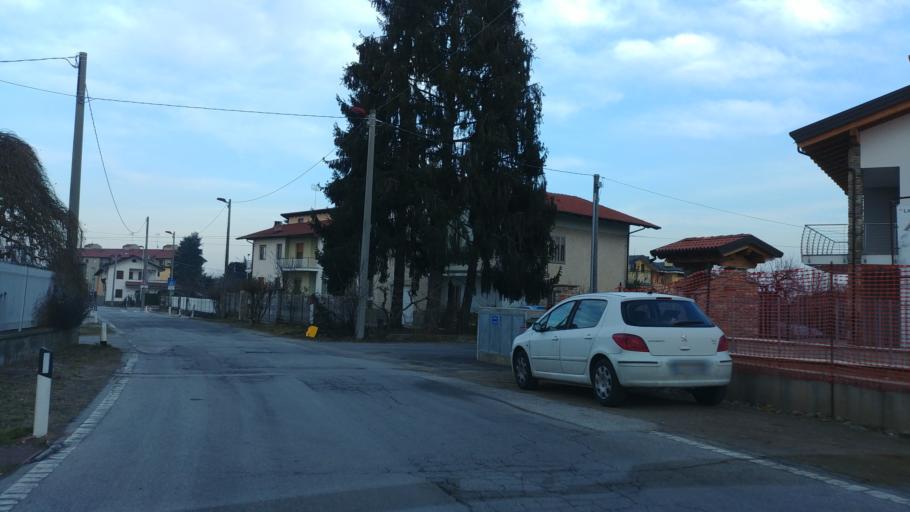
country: IT
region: Piedmont
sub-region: Provincia di Cuneo
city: Cuneo
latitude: 44.3995
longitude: 7.5289
